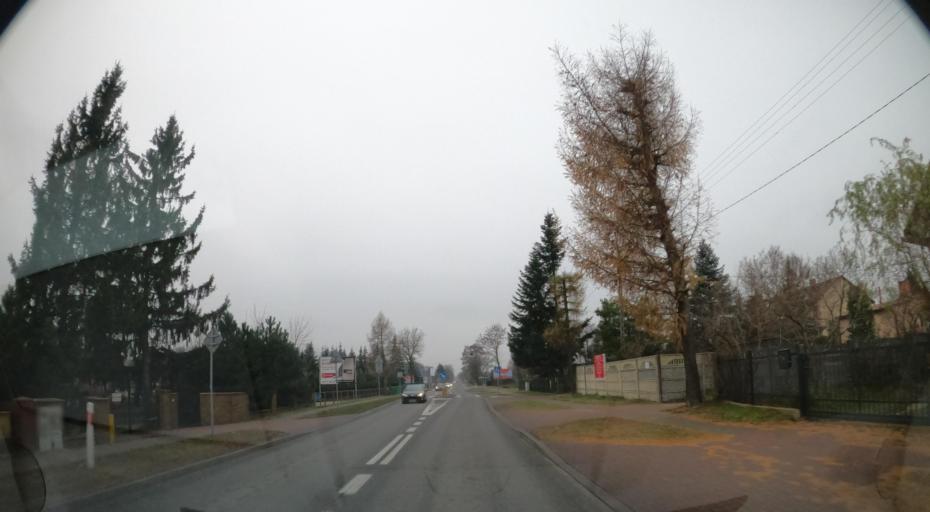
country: PL
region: Masovian Voivodeship
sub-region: Powiat radomski
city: Jastrzebia
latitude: 51.4282
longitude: 21.2320
